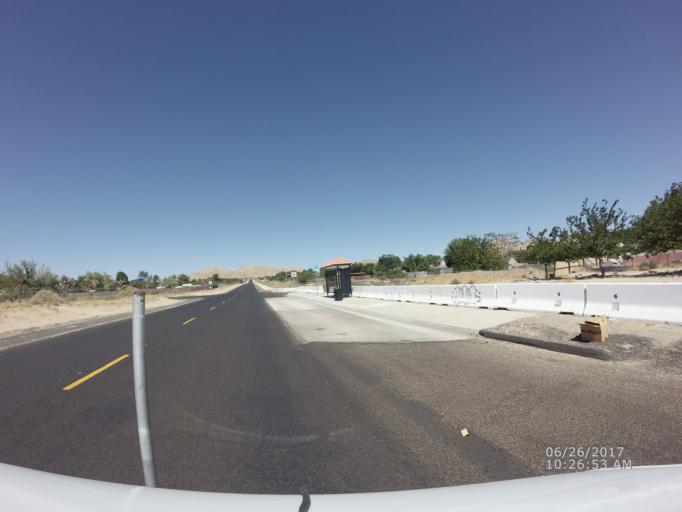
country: US
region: California
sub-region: Los Angeles County
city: Lake Los Angeles
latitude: 34.5946
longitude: -117.8306
